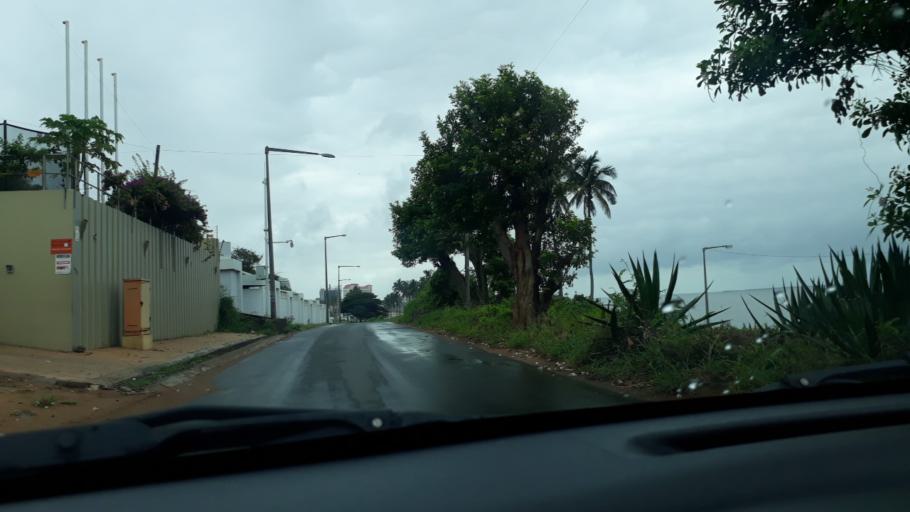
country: MZ
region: Maputo City
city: Maputo
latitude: -25.9697
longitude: 32.5992
